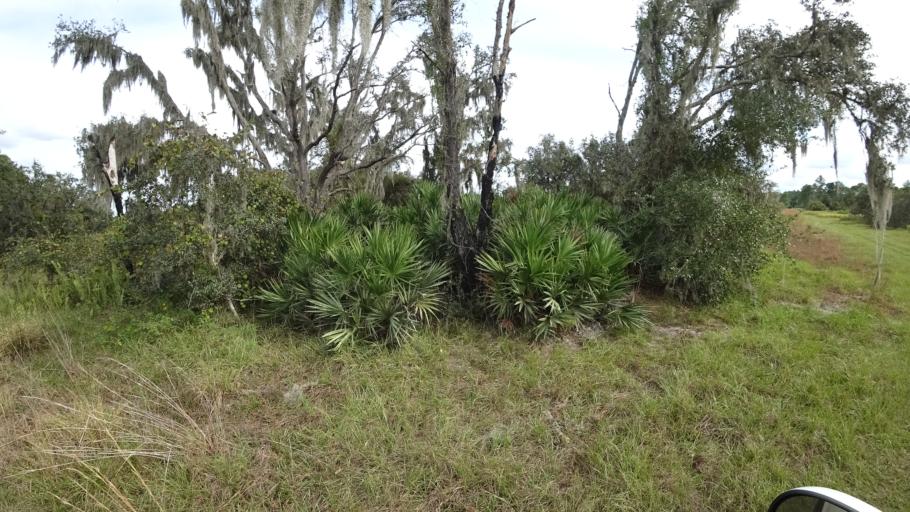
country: US
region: Florida
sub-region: Hillsborough County
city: Wimauma
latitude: 27.5516
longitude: -82.1362
